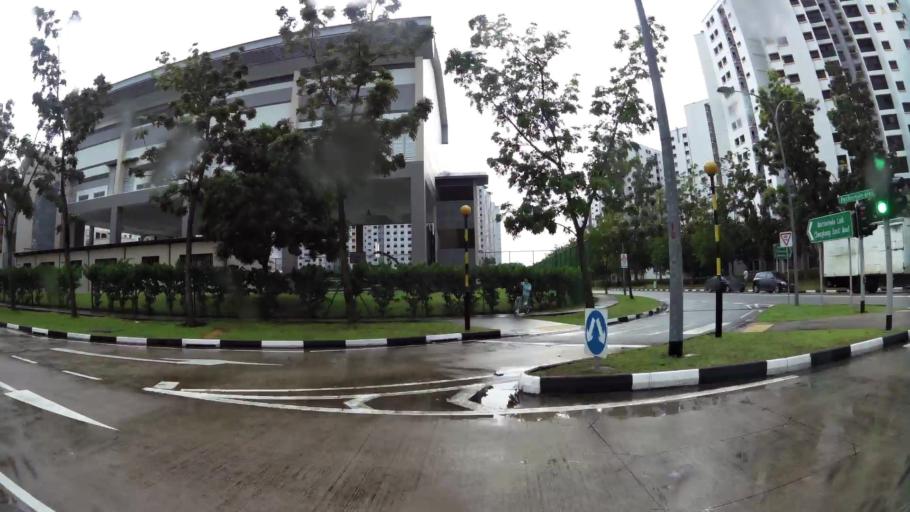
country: MY
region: Johor
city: Kampung Pasir Gudang Baru
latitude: 1.3904
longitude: 103.8896
